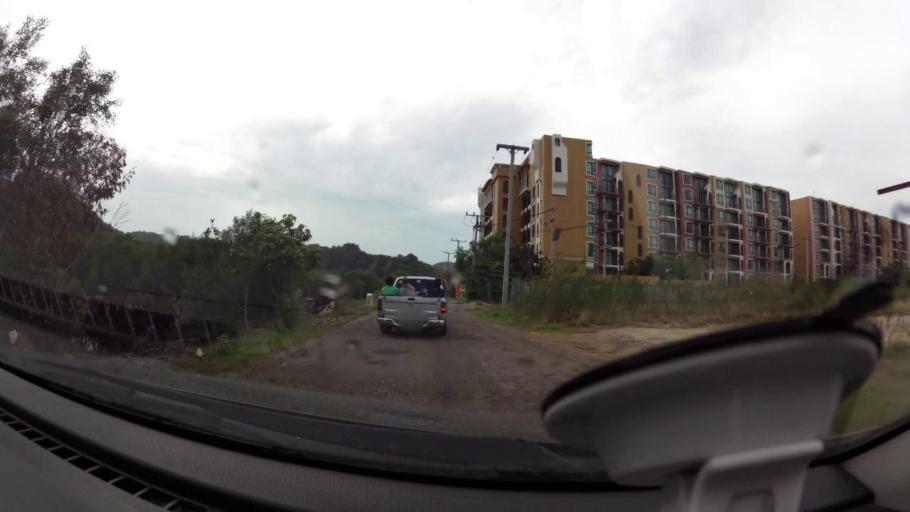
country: TH
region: Prachuap Khiri Khan
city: Pran Buri
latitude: 12.4195
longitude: 99.9804
